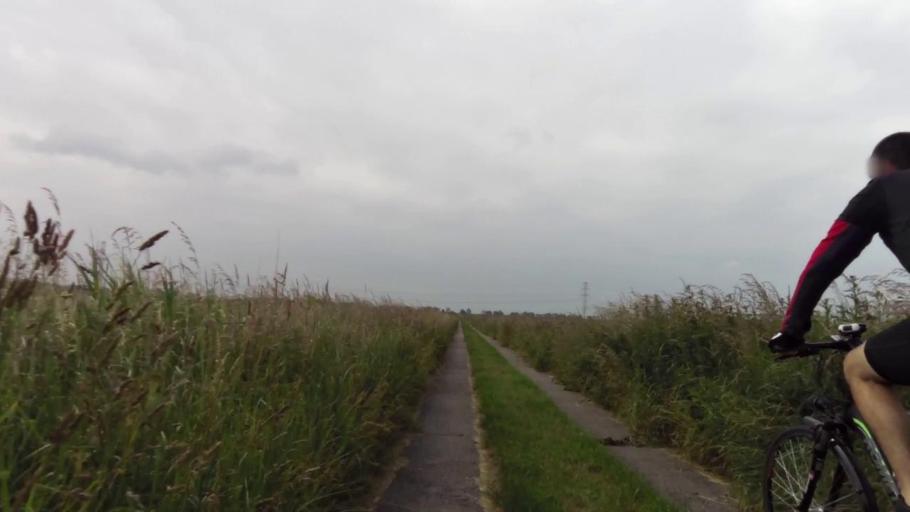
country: PL
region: West Pomeranian Voivodeship
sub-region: Powiat goleniowski
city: Stepnica
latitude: 53.5660
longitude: 14.6974
